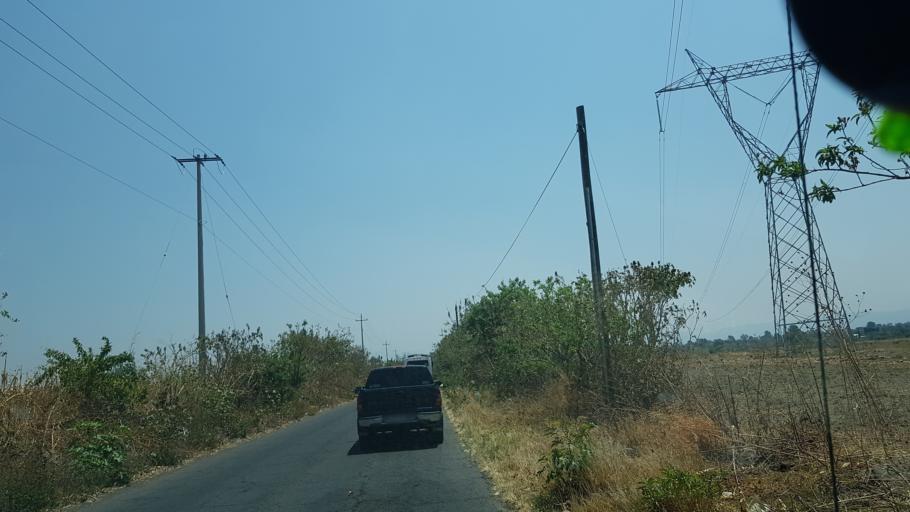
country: MX
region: Puebla
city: Tochimilco
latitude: 18.8897
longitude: -98.5244
